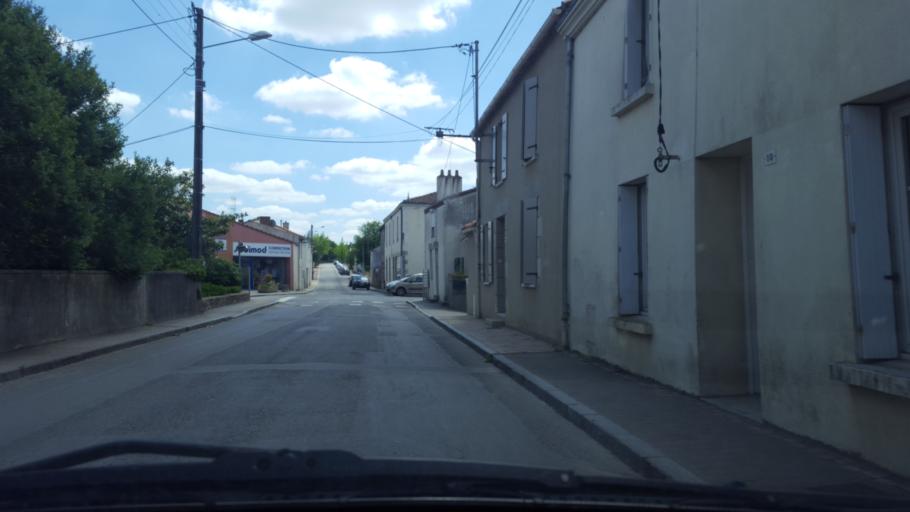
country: FR
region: Pays de la Loire
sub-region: Departement de la Vendee
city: Saint-Philbert-de-Bouaine
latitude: 46.9843
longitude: -1.5212
